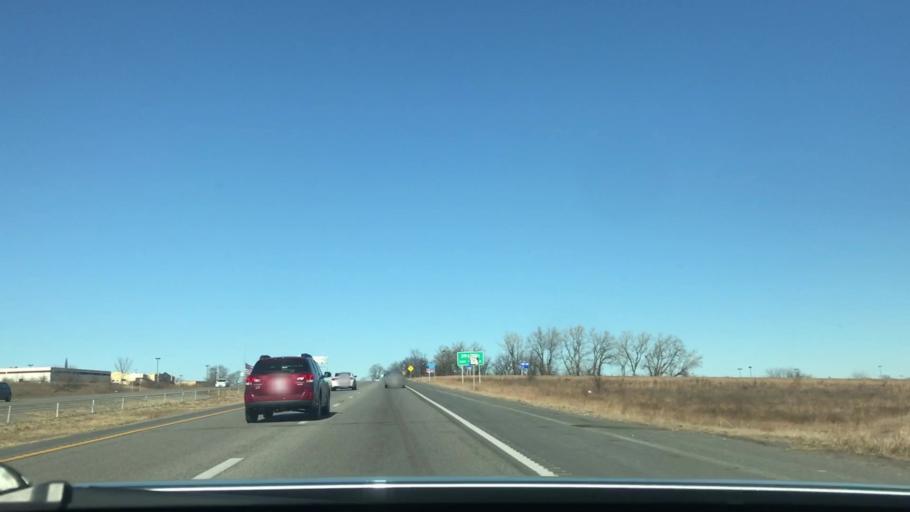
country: US
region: Missouri
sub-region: Jackson County
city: East Independence
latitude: 39.0431
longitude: -94.3625
